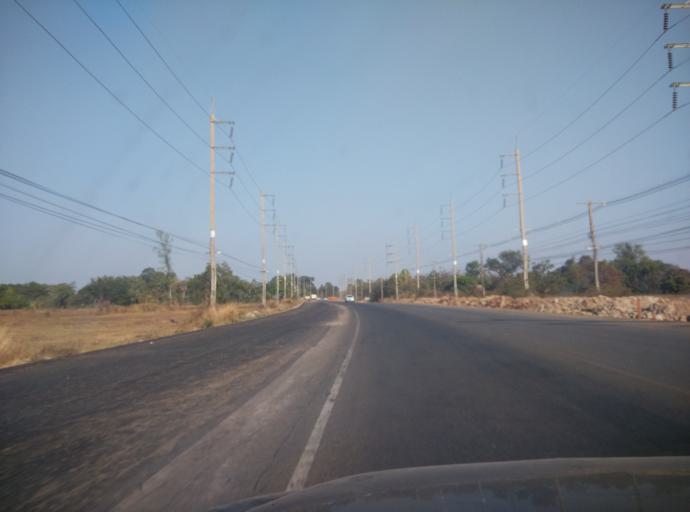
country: TH
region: Sisaket
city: Si Sa Ket
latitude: 15.1452
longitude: 104.2419
